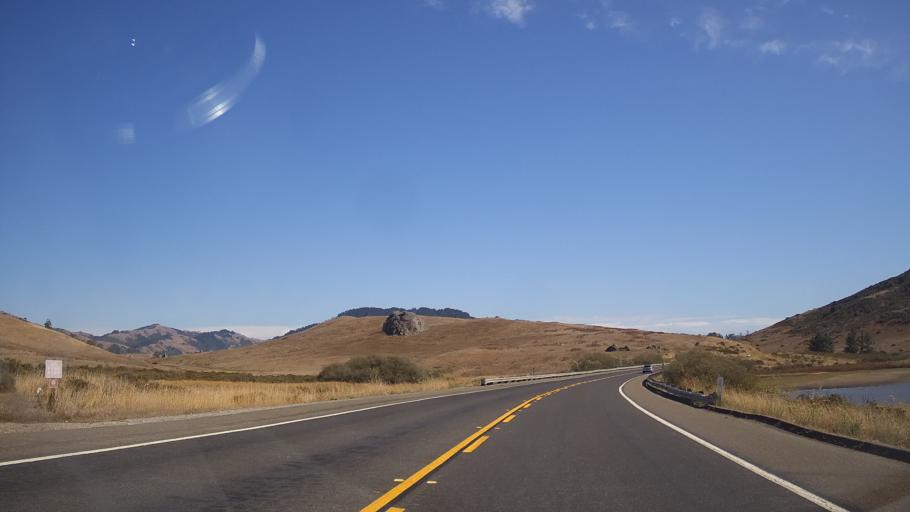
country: US
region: California
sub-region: Marin County
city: Lagunitas-Forest Knolls
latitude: 38.0869
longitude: -122.7244
